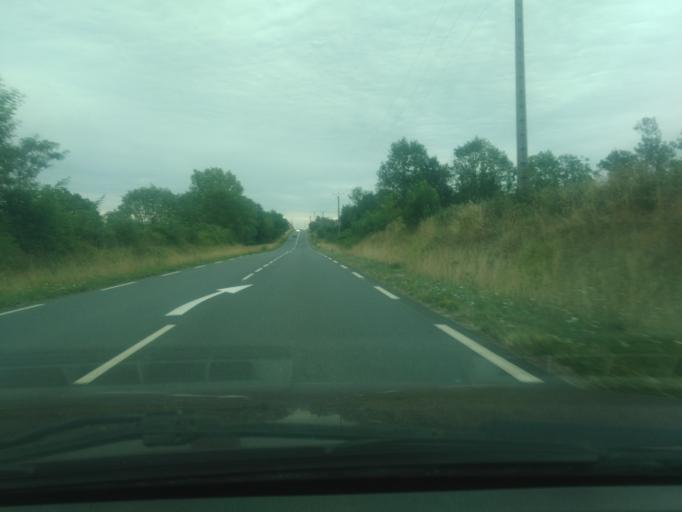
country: FR
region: Centre
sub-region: Departement de l'Indre
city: Le Pechereau
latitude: 46.6036
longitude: 1.6293
